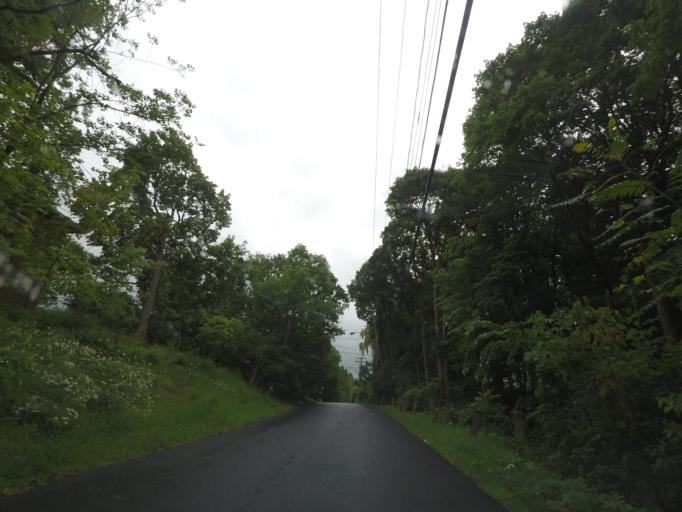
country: US
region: New York
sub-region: Rensselaer County
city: Rensselaer
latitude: 42.6335
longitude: -73.7359
